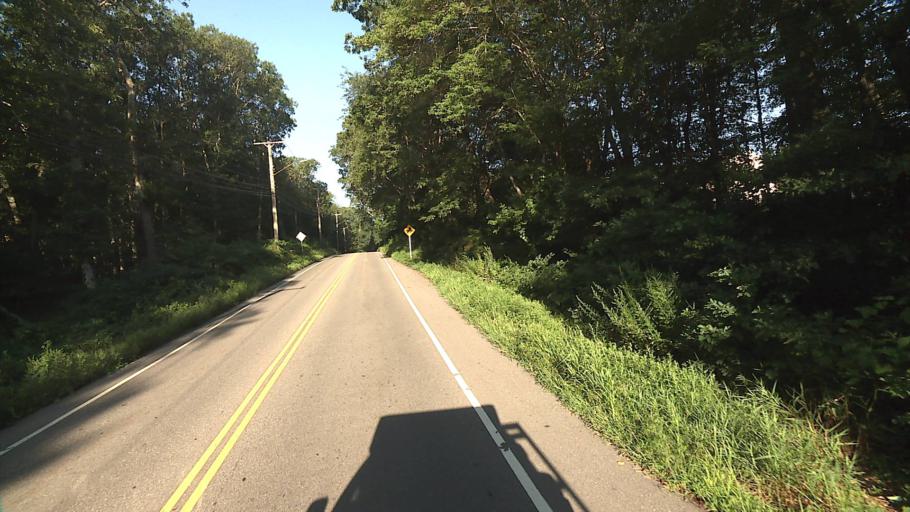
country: US
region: Connecticut
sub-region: New London County
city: Poquonock Bridge
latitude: 41.3514
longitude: -72.0044
